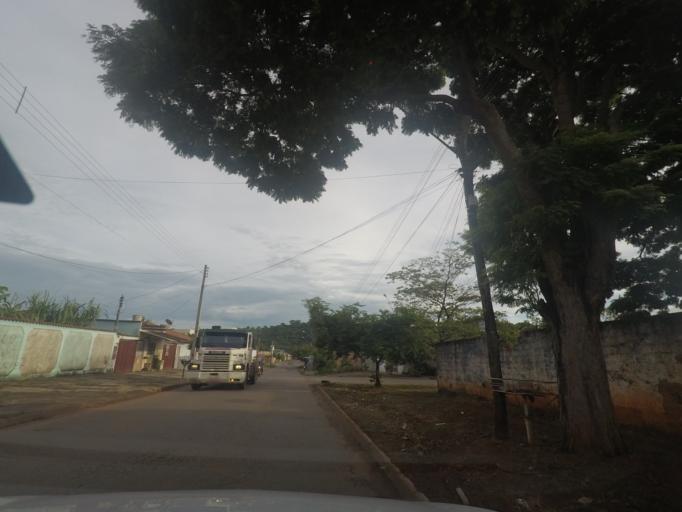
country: BR
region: Goias
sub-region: Goiania
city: Goiania
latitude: -16.6882
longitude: -49.3587
